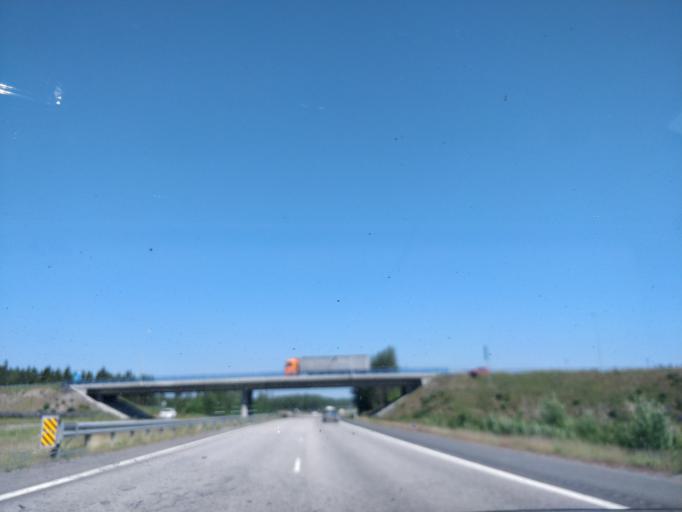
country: FI
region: Haeme
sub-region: Riihimaeki
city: Riihimaeki
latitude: 60.6870
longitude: 24.7510
